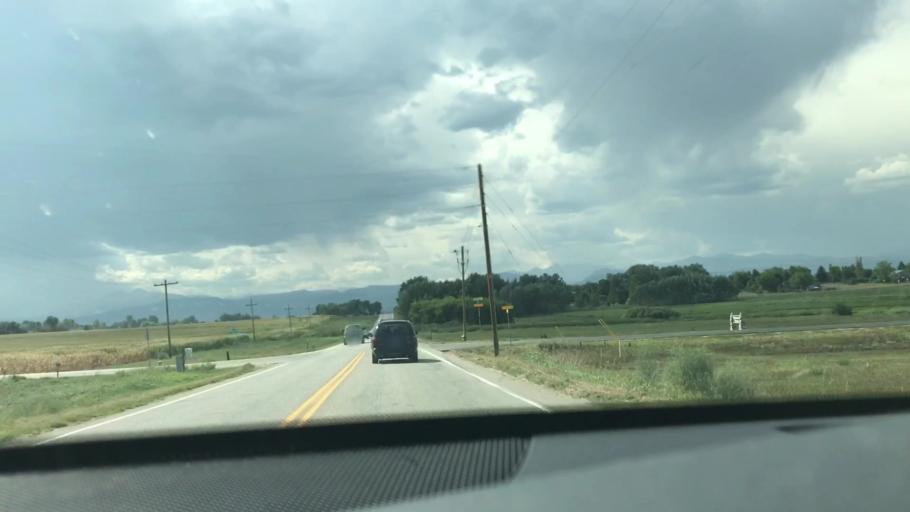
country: US
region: Colorado
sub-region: Larimer County
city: Loveland
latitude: 40.3785
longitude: -105.0012
